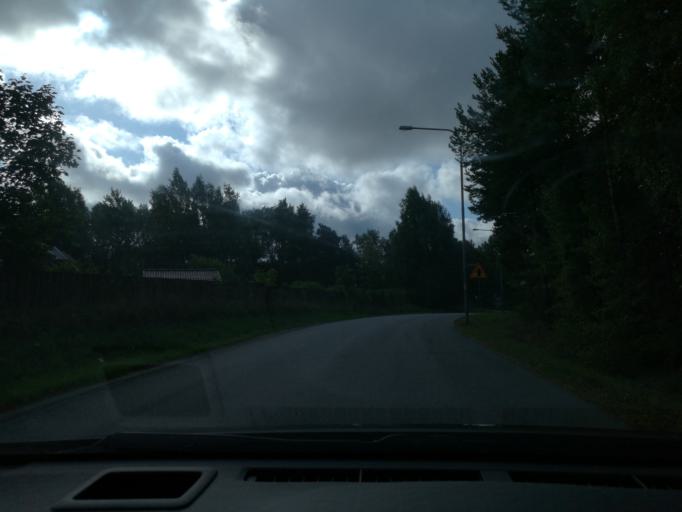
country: SE
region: Stockholm
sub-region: Vallentuna Kommun
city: Vallentuna
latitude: 59.5439
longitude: 18.0498
